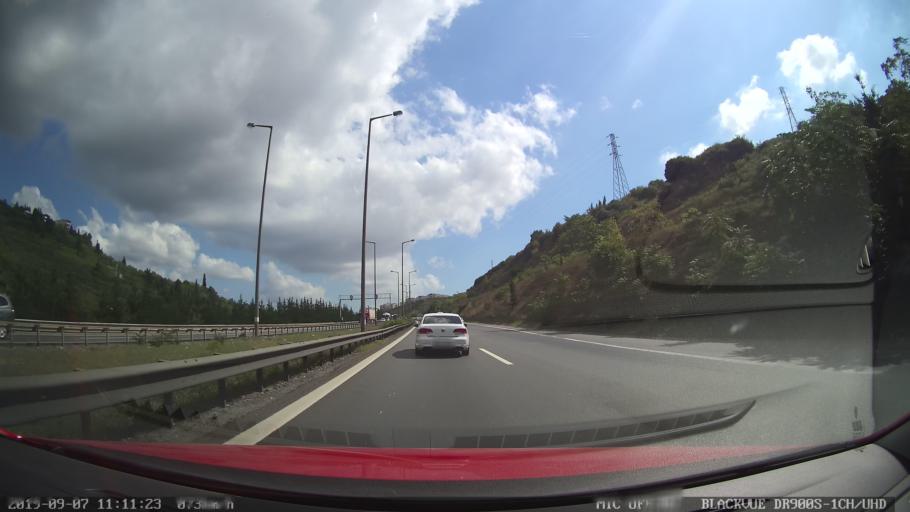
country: TR
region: Kocaeli
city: Izmit
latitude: 40.7763
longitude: 29.9150
